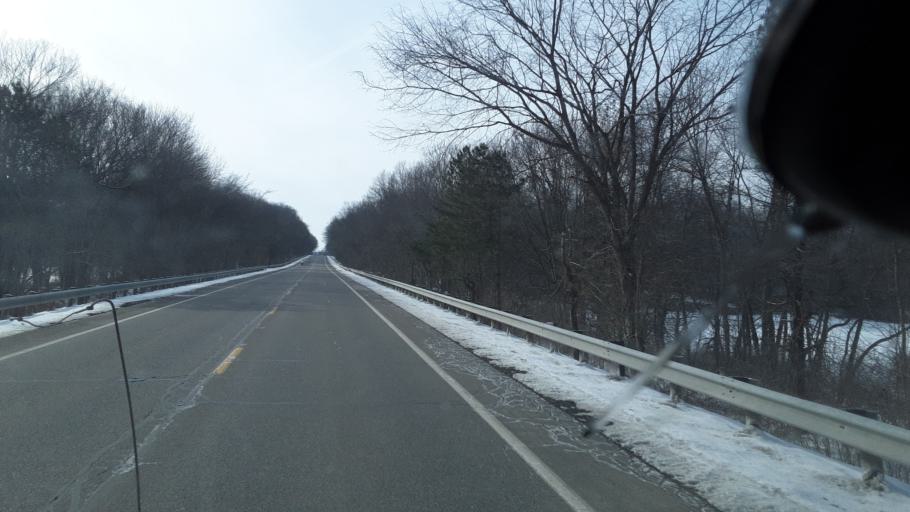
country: US
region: Ohio
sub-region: Stark County
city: Hartville
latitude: 41.0333
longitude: -81.2855
